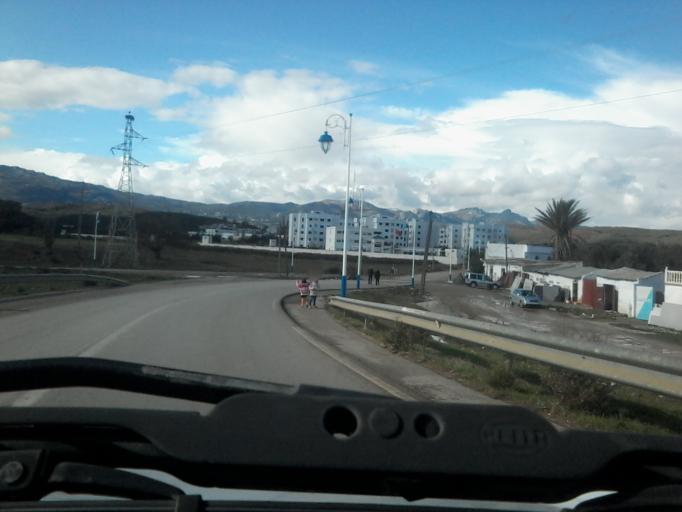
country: MA
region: Tanger-Tetouan
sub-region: Tetouan
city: Martil
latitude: 35.7026
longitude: -5.3555
